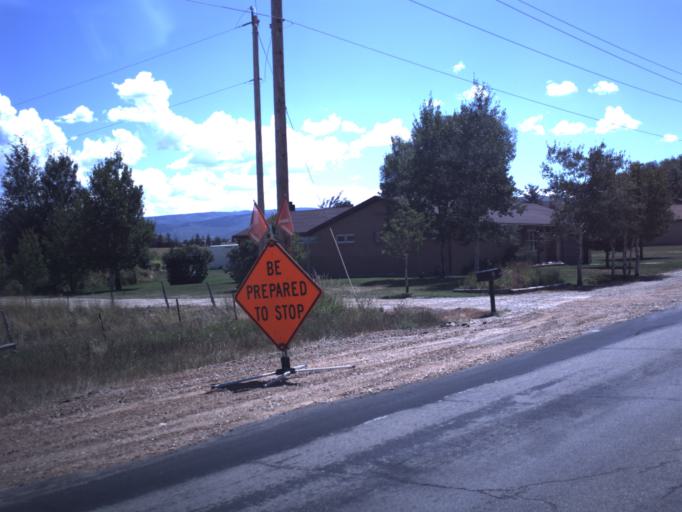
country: US
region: Utah
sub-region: Summit County
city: Francis
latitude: 40.6218
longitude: -111.2807
